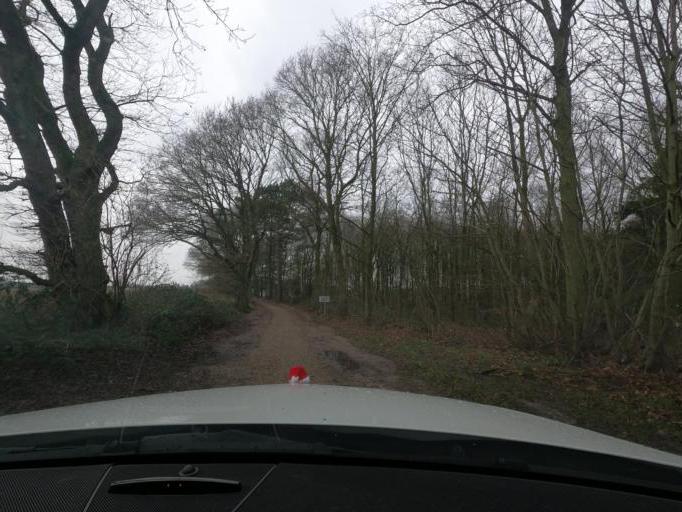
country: DK
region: South Denmark
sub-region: Haderslev Kommune
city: Starup
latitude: 55.2462
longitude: 9.5267
